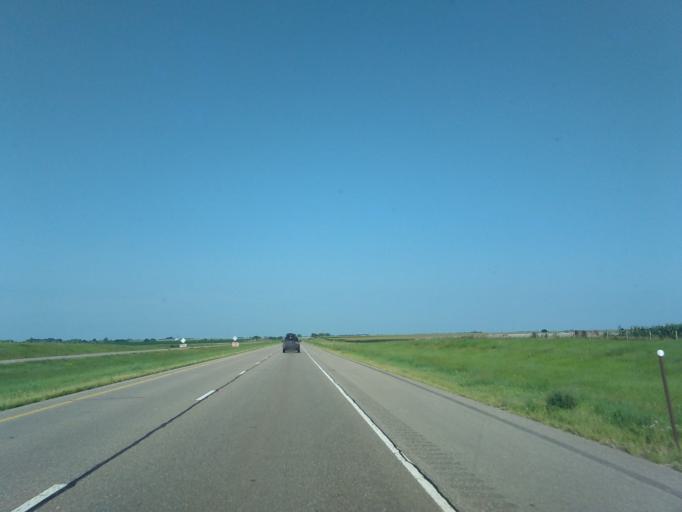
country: US
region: Nebraska
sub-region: Hall County
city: Grand Island
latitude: 40.8212
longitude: -98.2171
